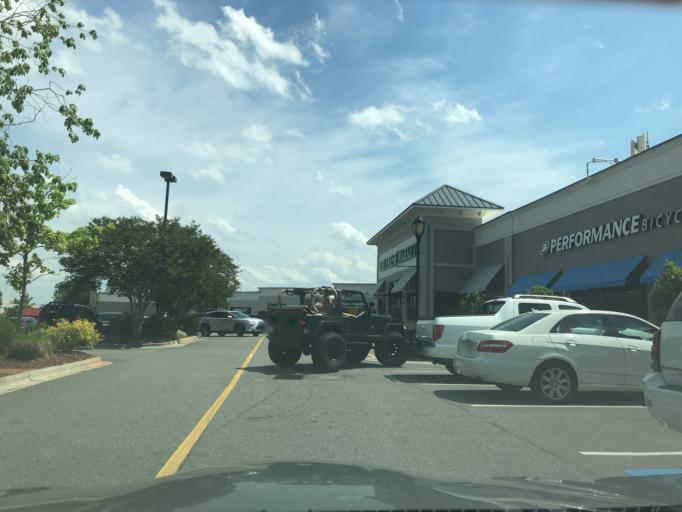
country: US
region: North Carolina
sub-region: Wake County
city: West Raleigh
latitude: 35.8692
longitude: -78.6227
